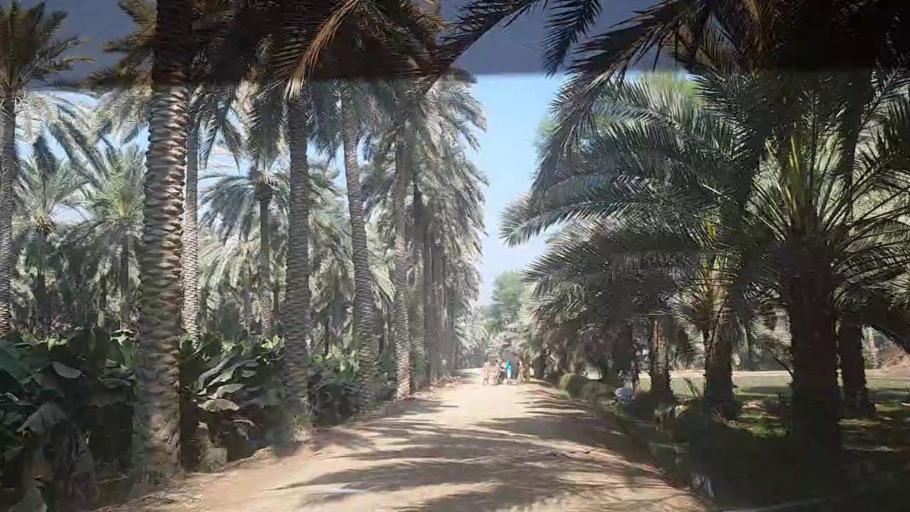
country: PK
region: Sindh
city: Khairpur
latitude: 27.4641
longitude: 68.7174
